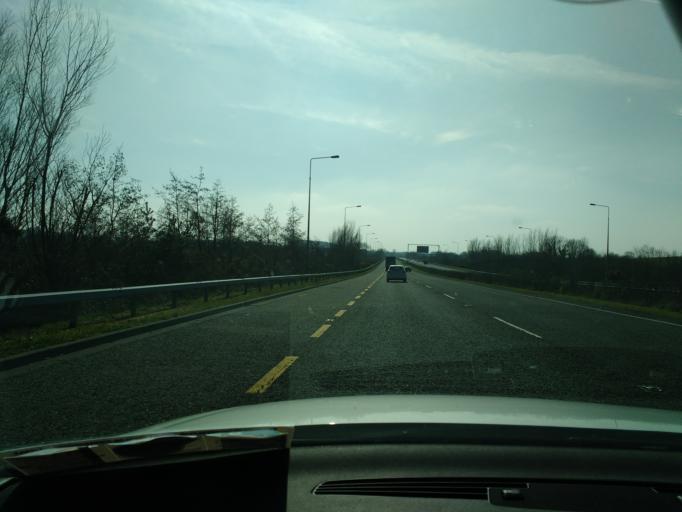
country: IE
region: Munster
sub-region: An Clar
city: Shannon
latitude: 52.7239
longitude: -8.8763
